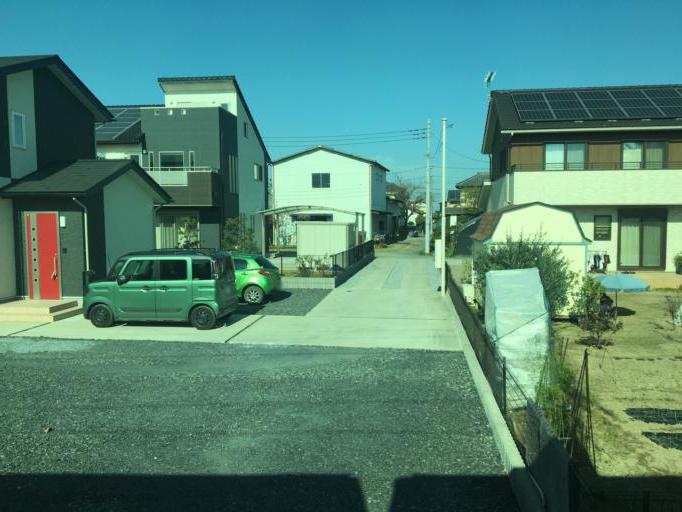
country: JP
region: Ibaraki
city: Yuki
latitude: 36.2968
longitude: 139.8913
